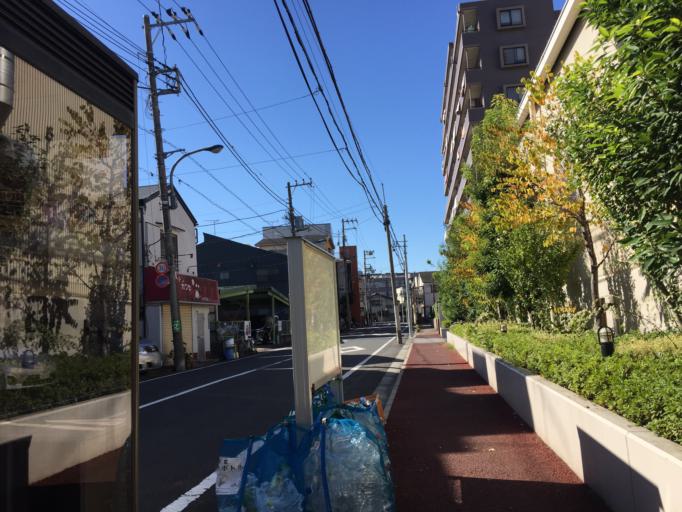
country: JP
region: Saitama
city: Kawaguchi
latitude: 35.7654
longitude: 139.7442
